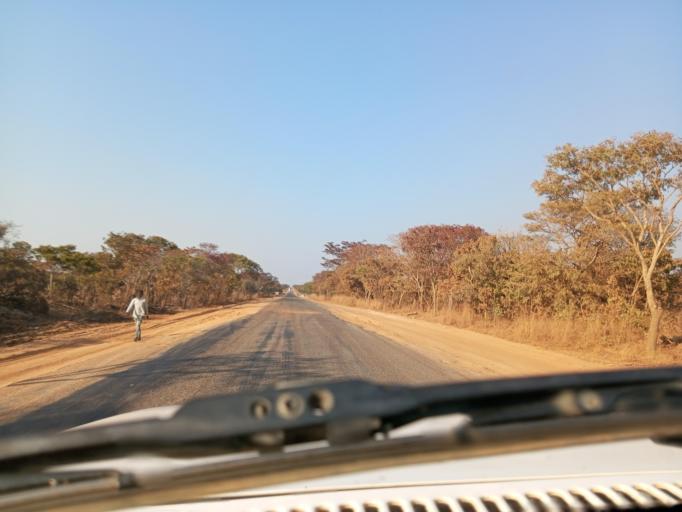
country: ZM
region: Northern
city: Mpika
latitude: -12.3967
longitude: 31.0906
